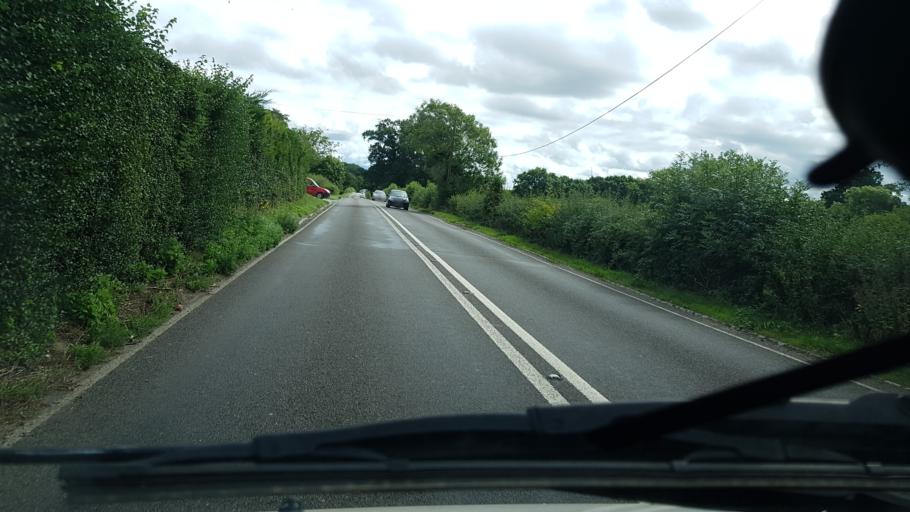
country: GB
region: England
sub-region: West Sussex
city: Rudgwick
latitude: 51.0864
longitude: -0.4331
